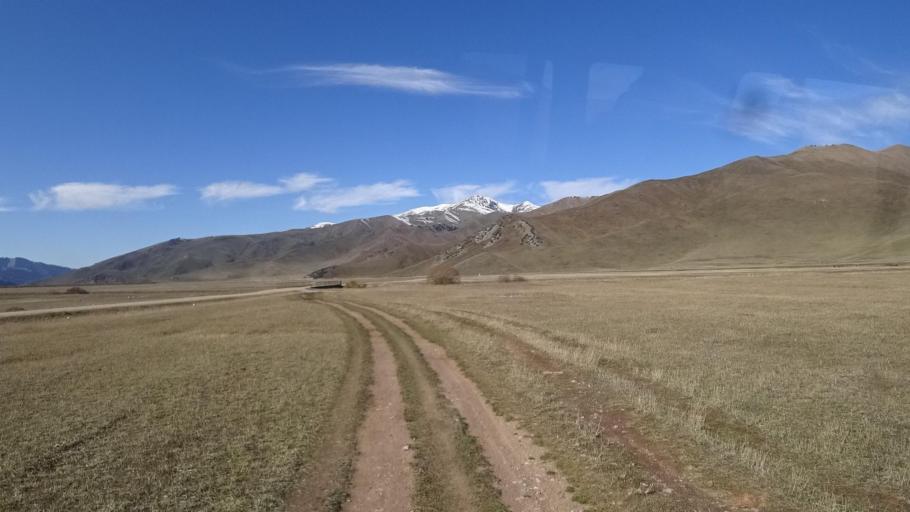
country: KZ
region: Almaty Oblysy
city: Kegen
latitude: 42.7468
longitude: 78.9925
